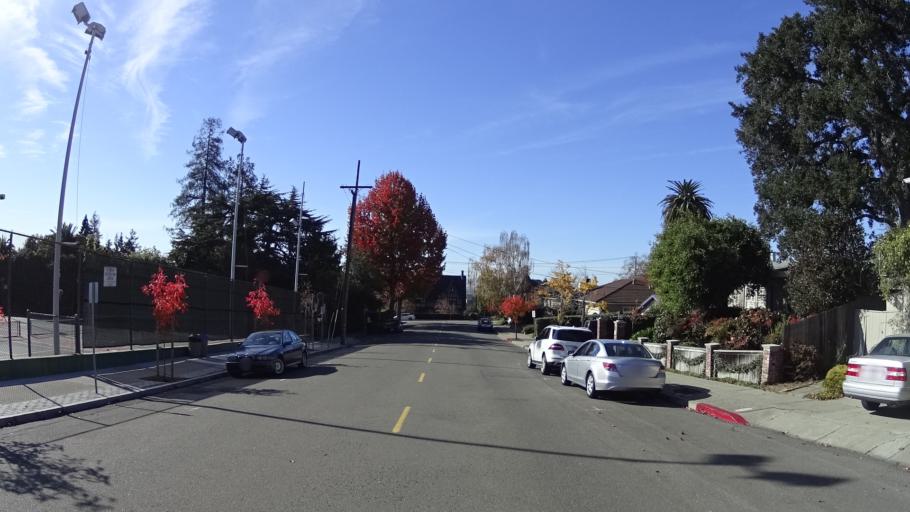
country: US
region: California
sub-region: Alameda County
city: Piedmont
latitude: 37.8243
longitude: -122.2338
